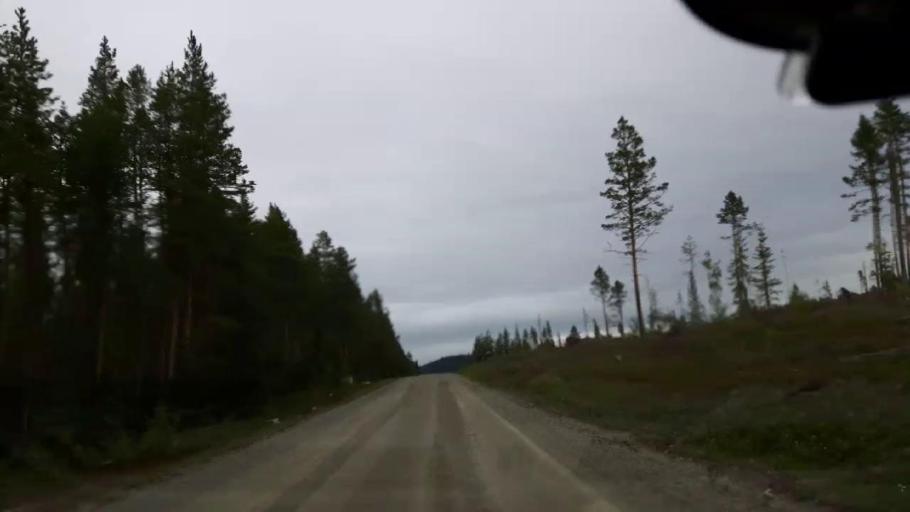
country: SE
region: Vaesternorrland
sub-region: Ange Kommun
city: Fransta
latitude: 62.8599
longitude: 16.0417
